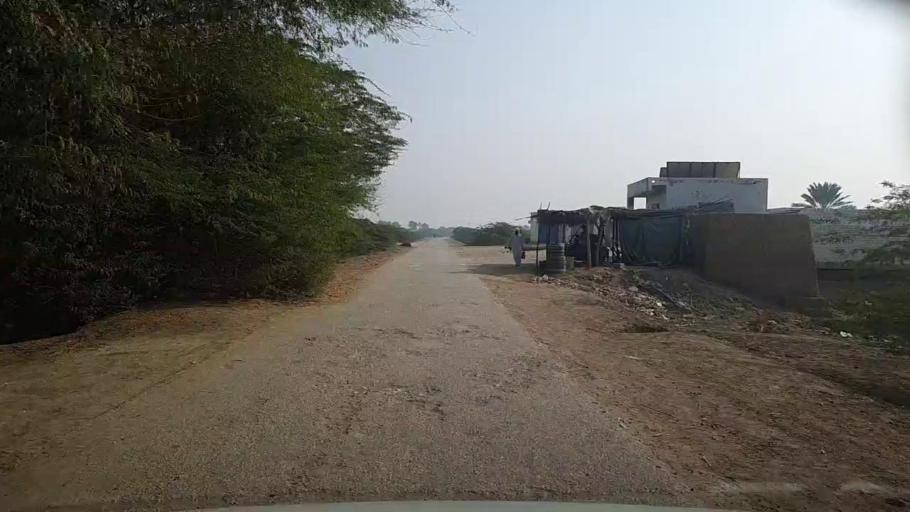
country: PK
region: Sindh
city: Kandiari
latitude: 27.0560
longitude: 68.4643
